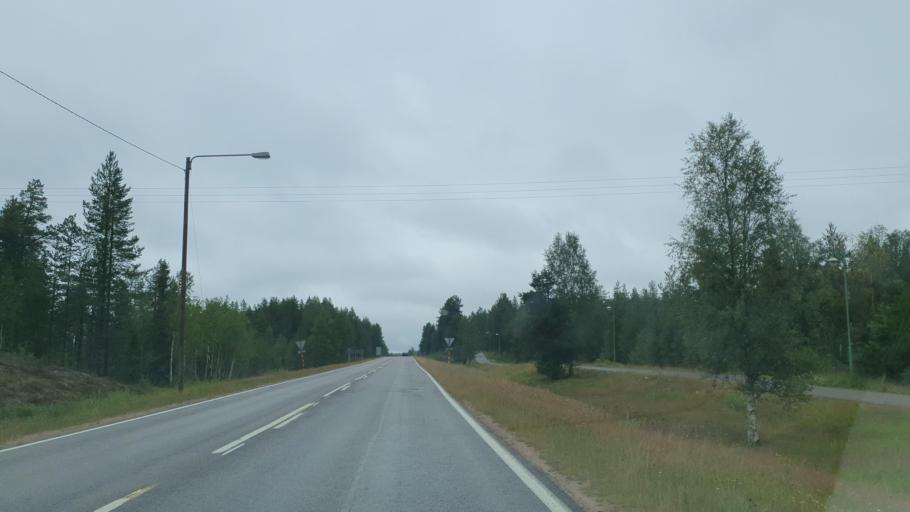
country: FI
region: Lapland
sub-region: Itae-Lappi
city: Kemijaervi
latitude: 66.7217
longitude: 27.3658
